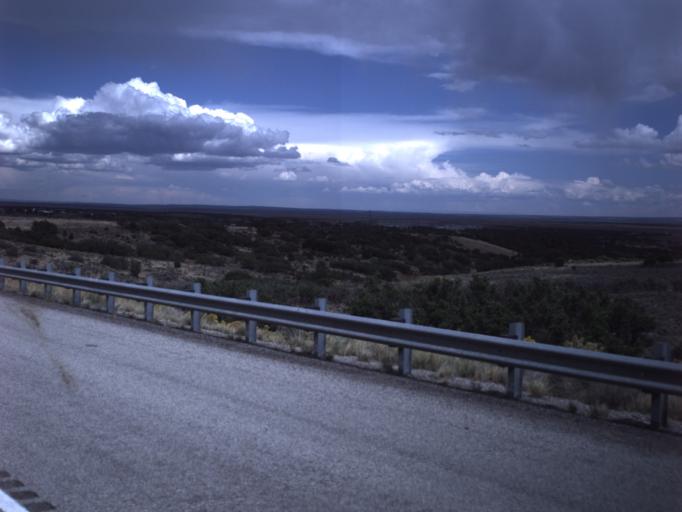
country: US
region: Utah
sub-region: San Juan County
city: Monticello
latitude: 37.8506
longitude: -109.3368
